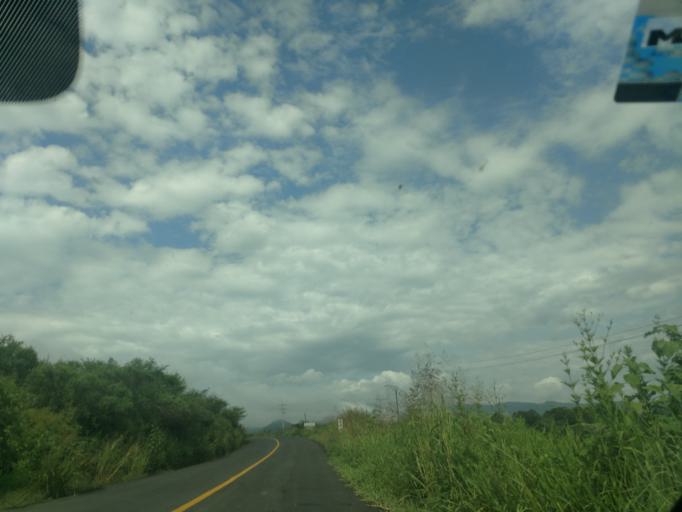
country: MX
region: Jalisco
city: El Salto
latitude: 20.4285
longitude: -104.4939
